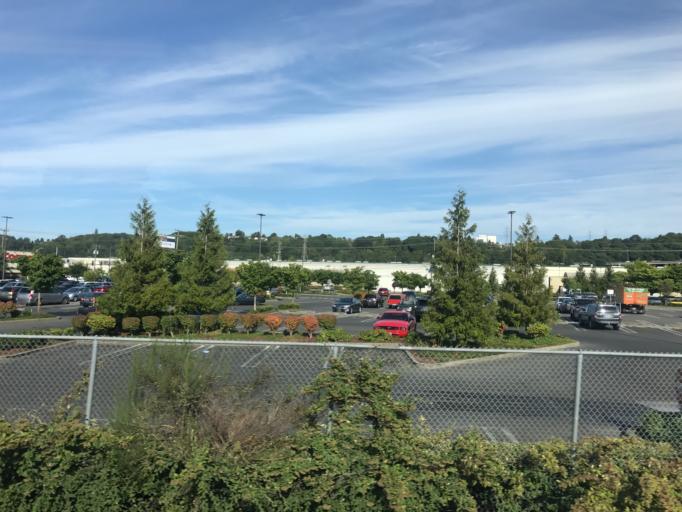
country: US
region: Washington
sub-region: King County
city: Seattle
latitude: 47.5638
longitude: -122.3315
